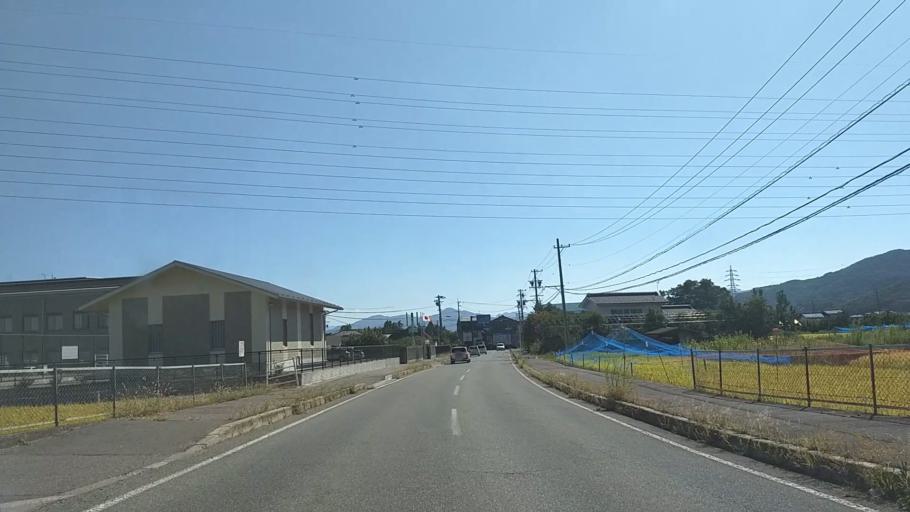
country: JP
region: Nagano
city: Nagano-shi
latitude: 36.6180
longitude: 138.1416
